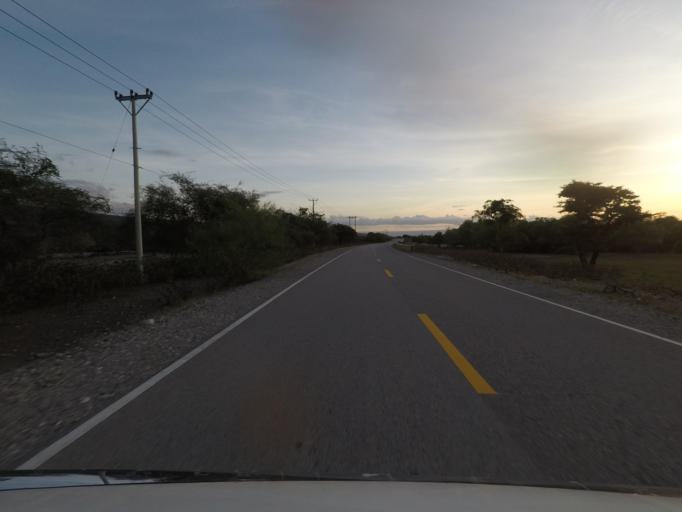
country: TL
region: Baucau
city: Baucau
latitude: -8.4411
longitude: 126.6553
